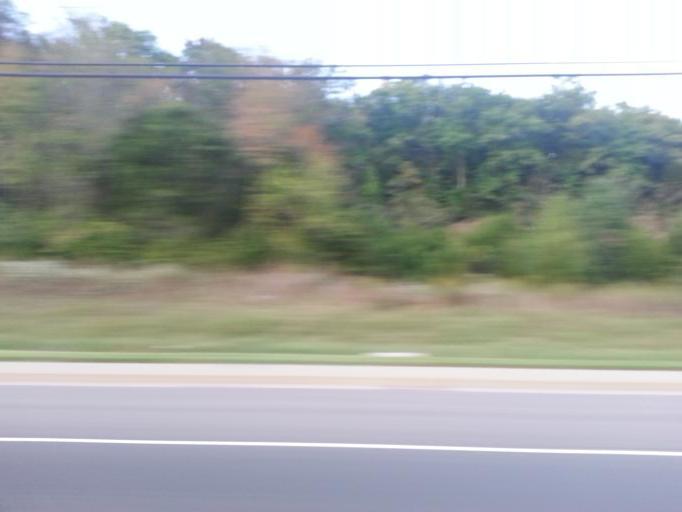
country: US
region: Tennessee
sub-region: Sevier County
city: Sevierville
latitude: 35.8879
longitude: -83.5754
